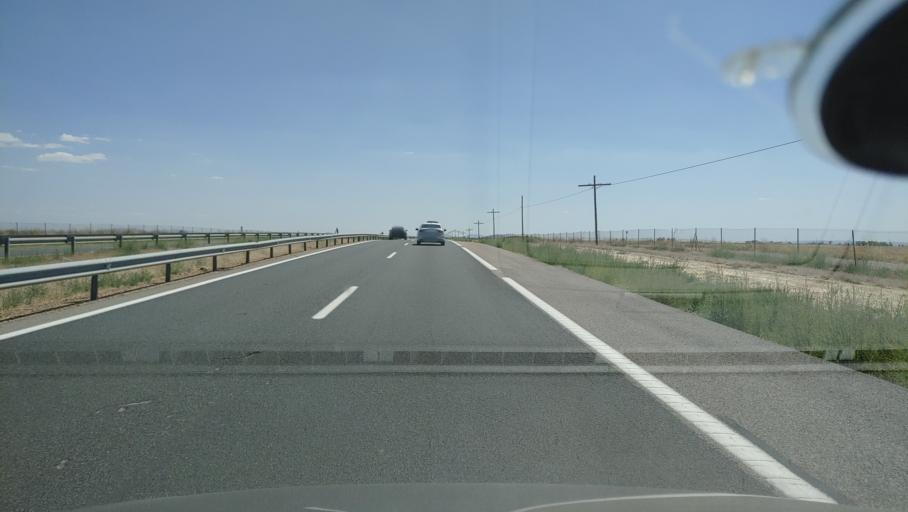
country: ES
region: Castille-La Mancha
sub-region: Provincia de Ciudad Real
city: Villarta de San Juan
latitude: 39.1541
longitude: -3.3883
